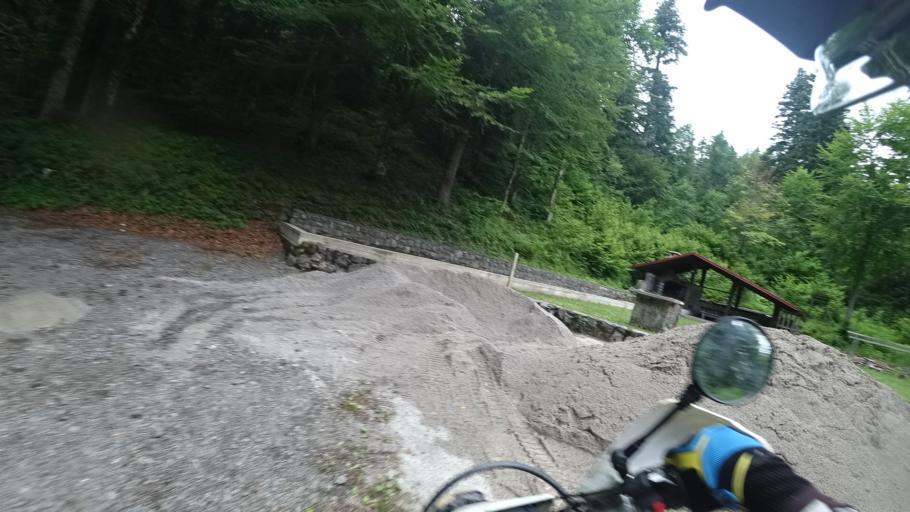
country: SI
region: Osilnica
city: Osilnica
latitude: 45.4860
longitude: 14.6782
